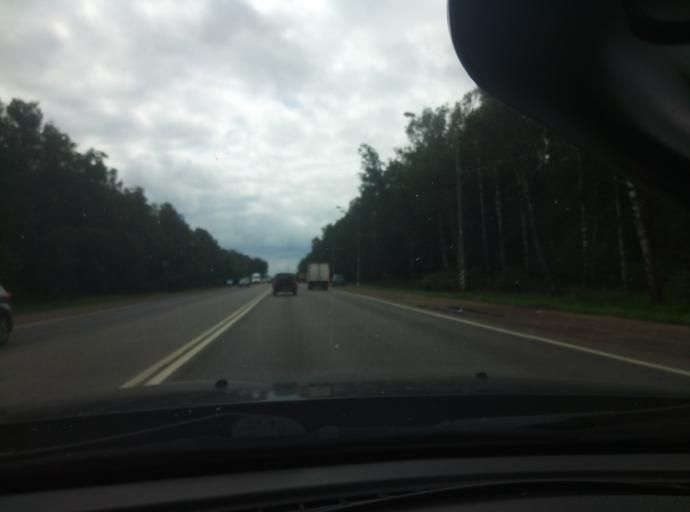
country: RU
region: Kaluga
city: Obninsk
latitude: 55.0843
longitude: 36.6317
